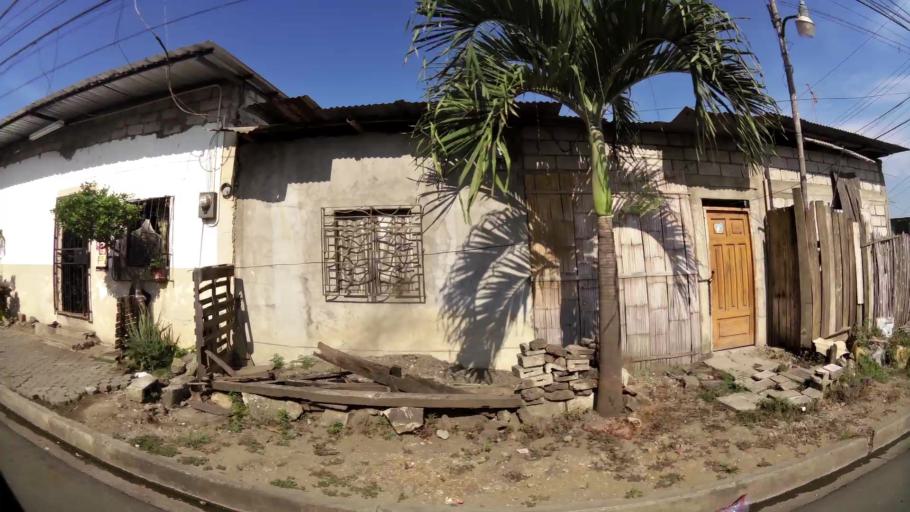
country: EC
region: Guayas
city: Eloy Alfaro
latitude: -2.0861
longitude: -79.9260
